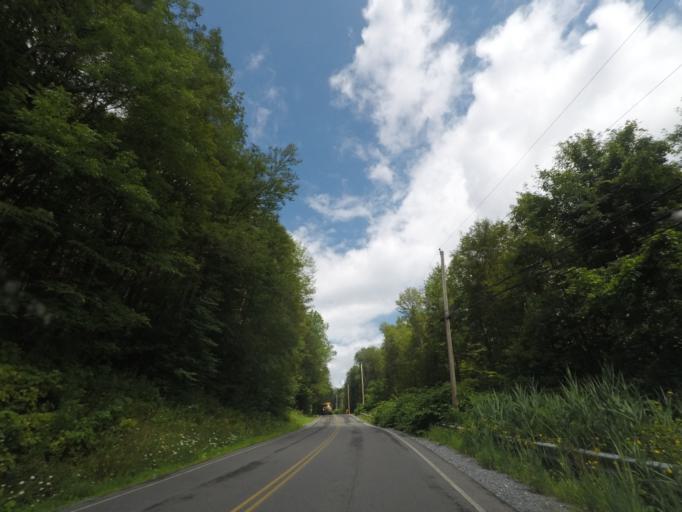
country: US
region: New York
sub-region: Rensselaer County
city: Averill Park
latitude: 42.6881
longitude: -73.3879
